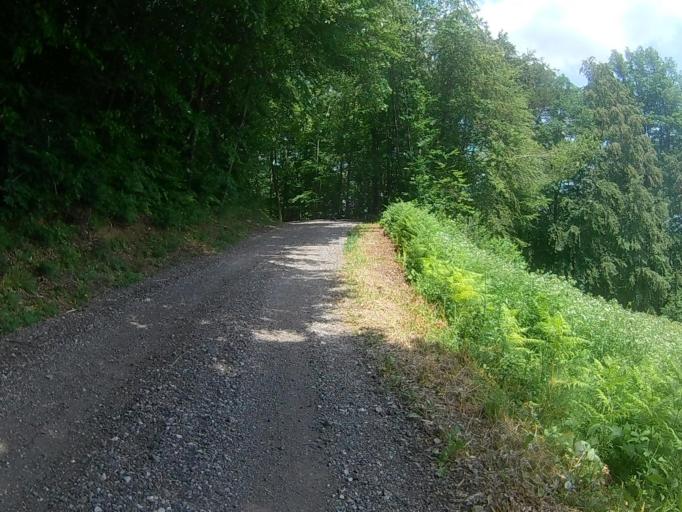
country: SI
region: Kungota
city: Zgornja Kungota
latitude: 46.6237
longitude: 15.6121
